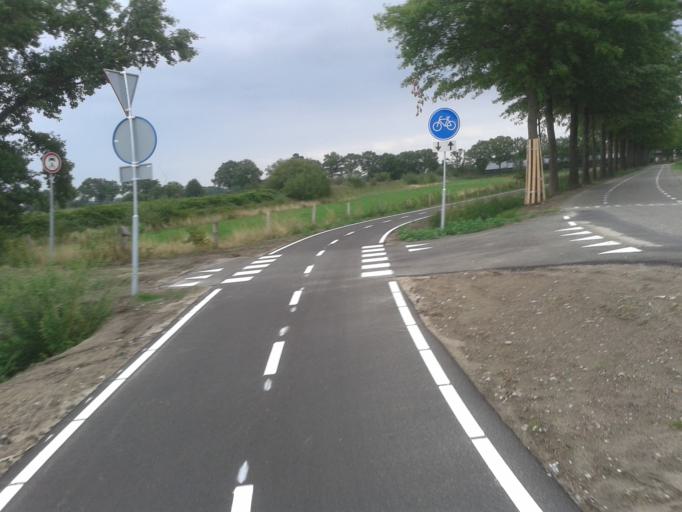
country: NL
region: North Brabant
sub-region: Gemeente Oisterwijk
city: Oisterwijk
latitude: 51.5184
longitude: 5.1902
